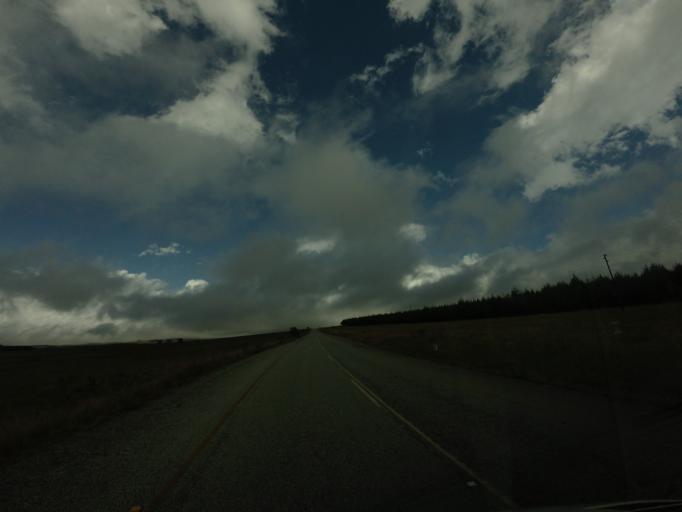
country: ZA
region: Mpumalanga
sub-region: Ehlanzeni District
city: Graksop
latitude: -24.8566
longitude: 30.8716
